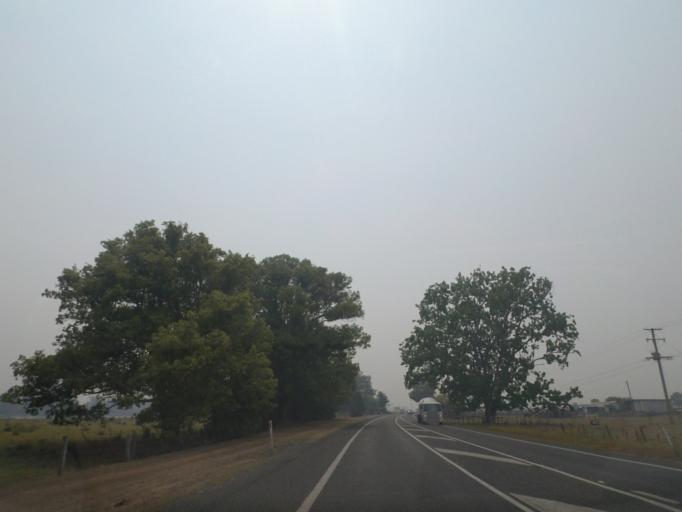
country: AU
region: New South Wales
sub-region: Clarence Valley
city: Maclean
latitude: -29.5647
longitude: 153.1045
